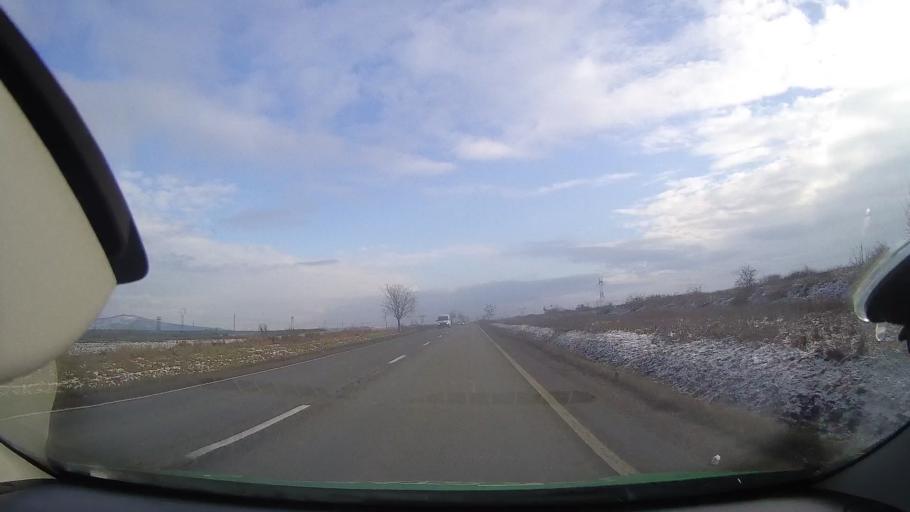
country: RO
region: Mures
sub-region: Comuna Cuci
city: Cuci
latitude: 46.4574
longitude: 24.1740
